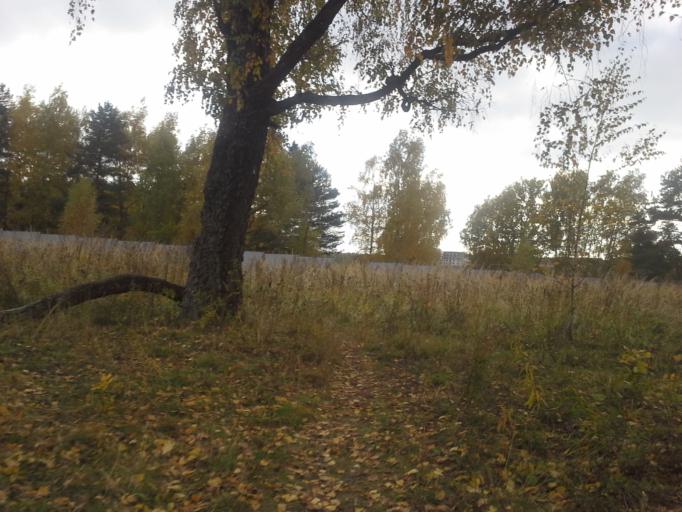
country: RU
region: Moskovskaya
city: Kommunarka
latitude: 55.5564
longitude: 37.5167
